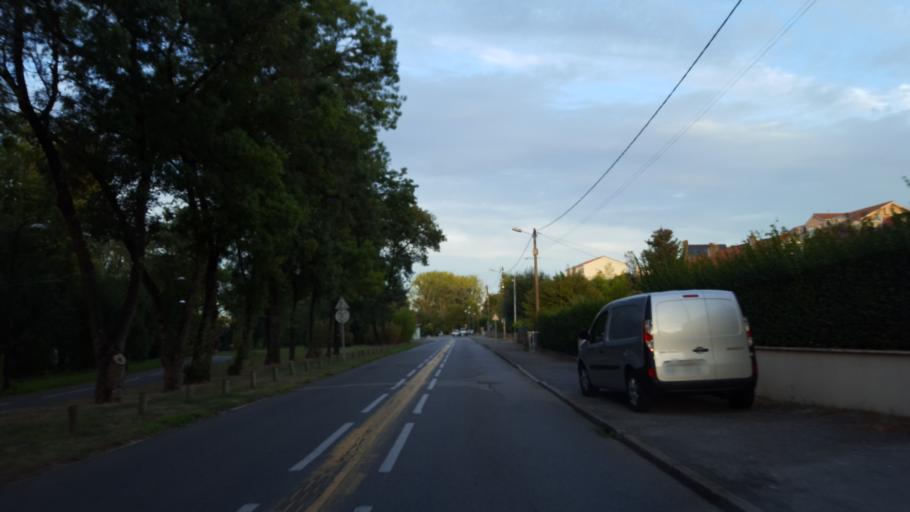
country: FR
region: Pays de la Loire
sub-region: Departement de la Loire-Atlantique
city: Basse-Goulaine
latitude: 47.2158
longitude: -1.4731
